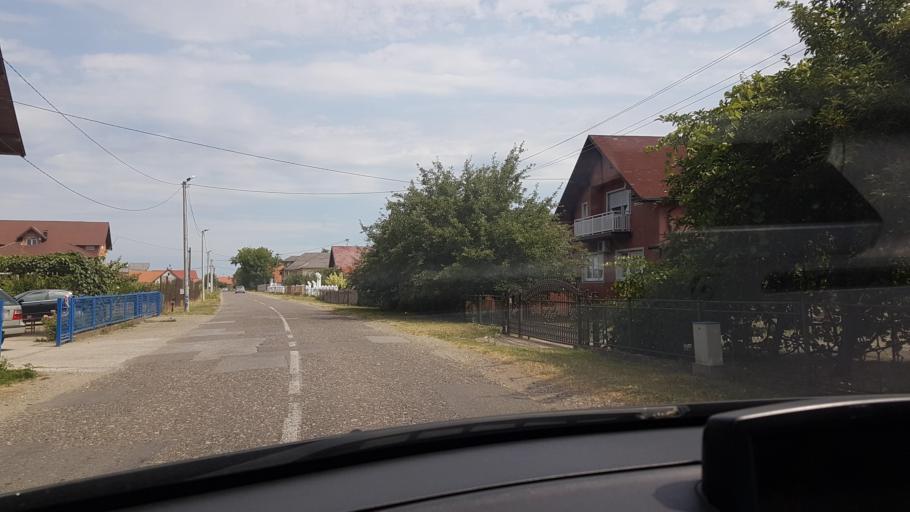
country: BA
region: Republika Srpska
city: Dvorovi
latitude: 44.8064
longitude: 19.2182
